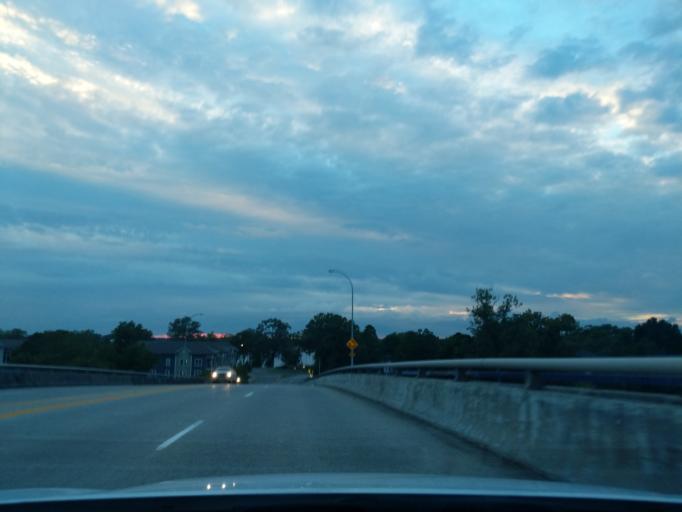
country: US
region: Tennessee
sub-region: Shelby County
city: Memphis
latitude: 35.1586
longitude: -90.0531
